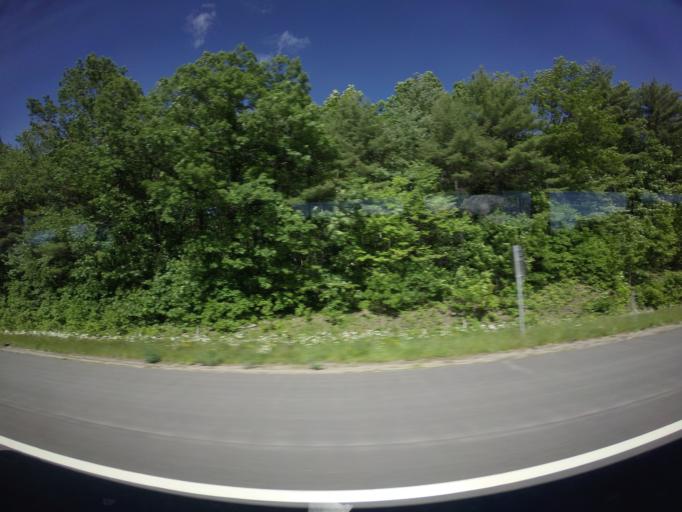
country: US
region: New Hampshire
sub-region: Rockingham County
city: Londonderry
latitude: 42.9254
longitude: -71.3771
